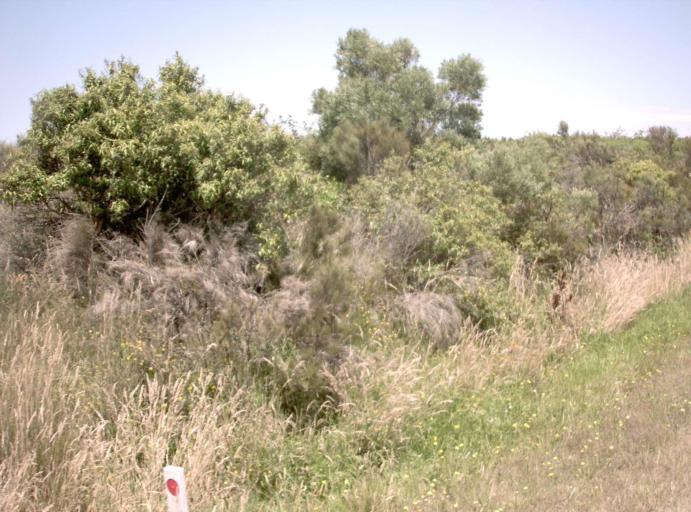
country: AU
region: Victoria
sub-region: Bass Coast
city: North Wonthaggi
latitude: -38.6151
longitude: 145.9678
